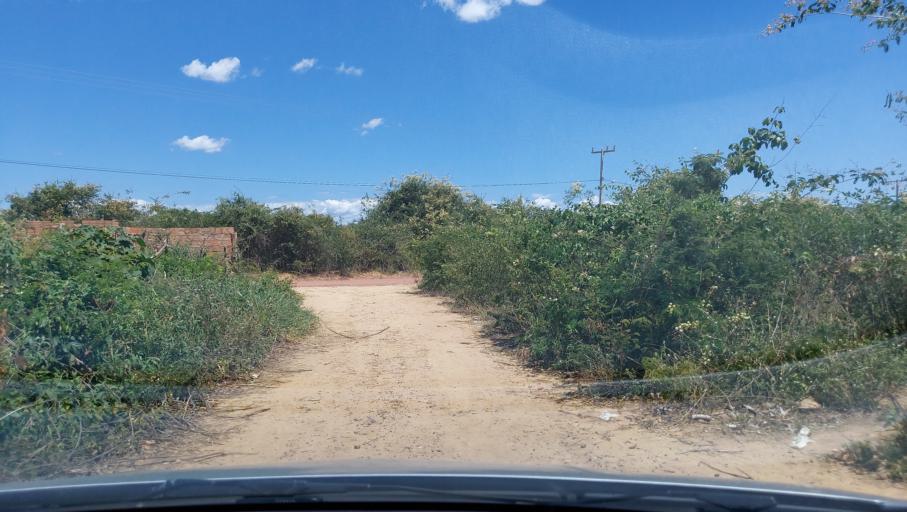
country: BR
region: Bahia
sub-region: Oliveira Dos Brejinhos
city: Beira Rio
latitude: -12.0066
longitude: -42.6357
